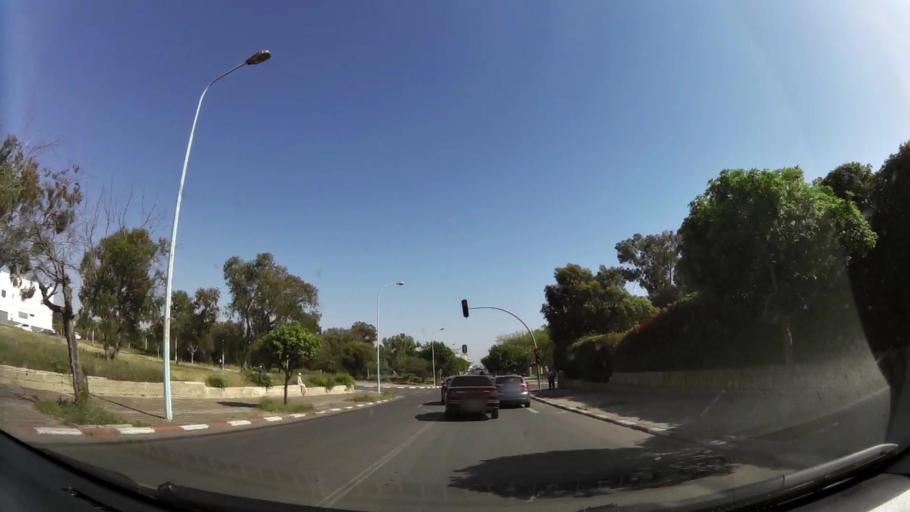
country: MA
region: Souss-Massa-Draa
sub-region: Agadir-Ida-ou-Tnan
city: Agadir
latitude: 30.4209
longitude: -9.5923
